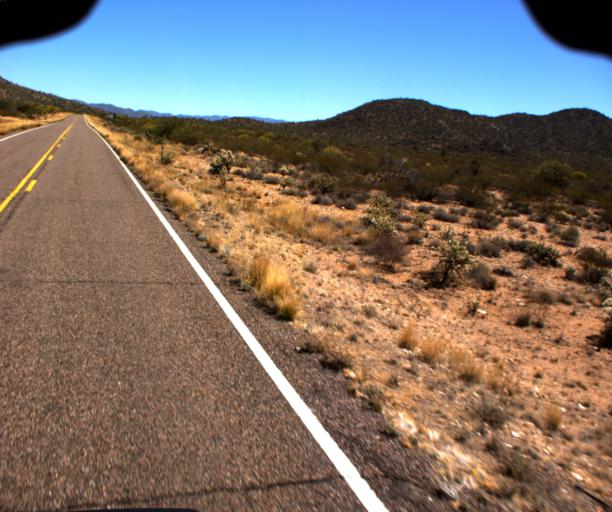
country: US
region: Arizona
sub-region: Yavapai County
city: Congress
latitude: 34.0973
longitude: -113.0005
